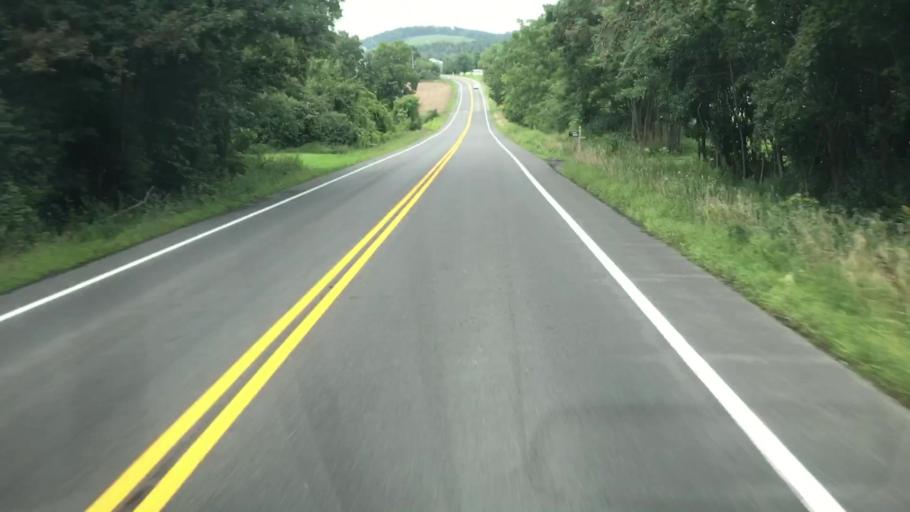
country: US
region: New York
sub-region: Onondaga County
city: Elbridge
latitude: 43.0035
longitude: -76.4398
